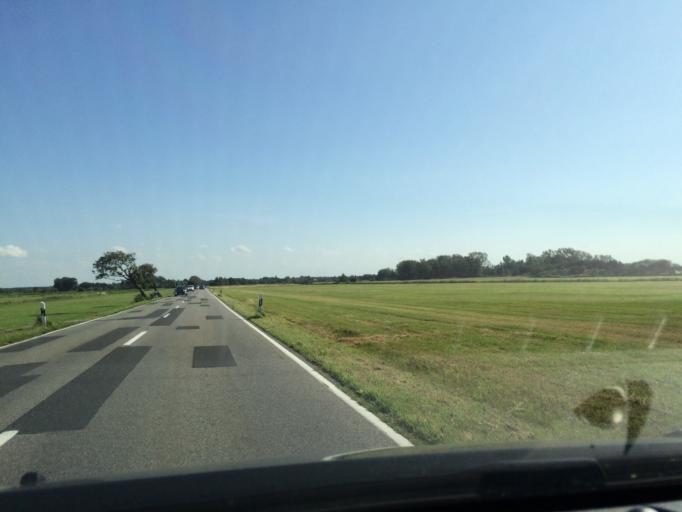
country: DE
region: Mecklenburg-Vorpommern
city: Zingst
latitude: 54.3924
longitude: 12.6775
